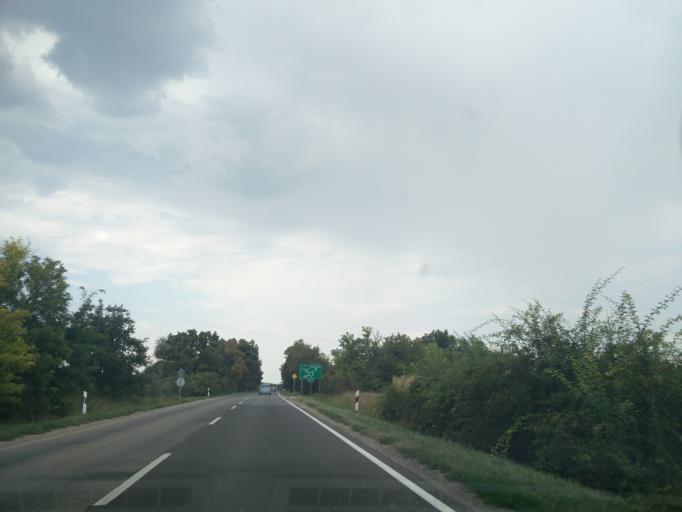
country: HU
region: Fejer
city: Polgardi
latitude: 47.0638
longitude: 18.3092
